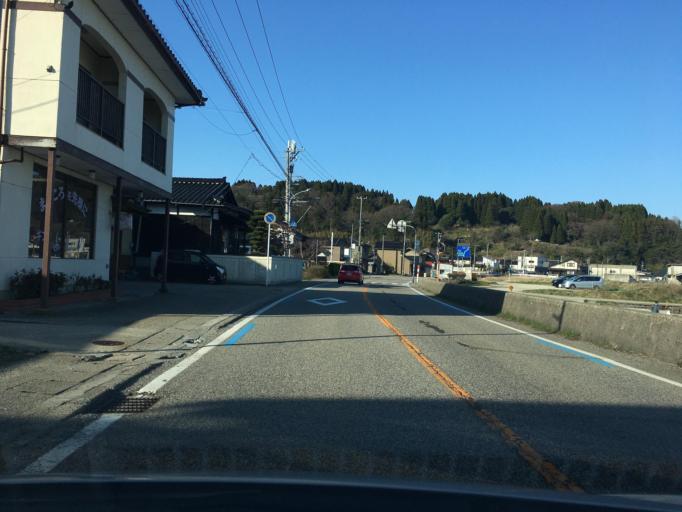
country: JP
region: Toyama
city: Himi
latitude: 36.9108
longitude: 137.0176
